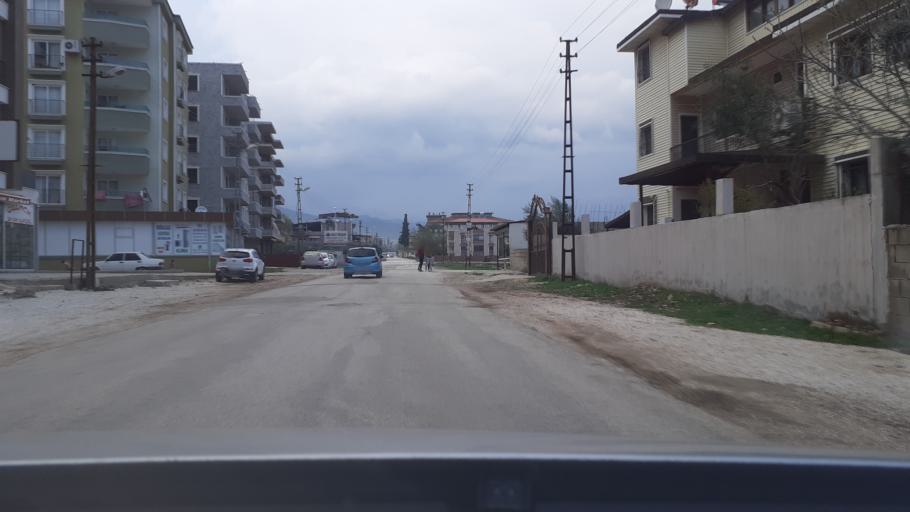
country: TR
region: Hatay
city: Kirikhan
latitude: 36.4841
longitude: 36.3555
